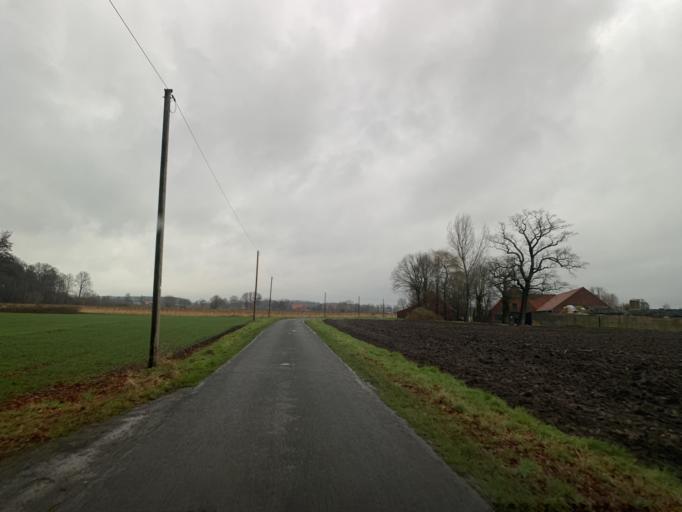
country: DE
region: North Rhine-Westphalia
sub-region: Regierungsbezirk Munster
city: Nordwalde
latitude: 52.0872
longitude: 7.5141
